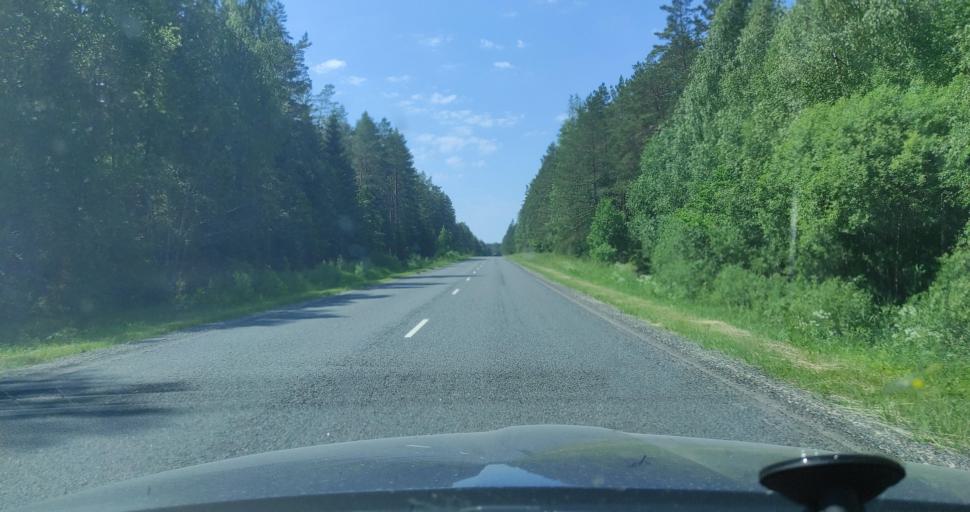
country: LV
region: Salacgrivas
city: Ainazi
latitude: 57.8544
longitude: 24.4742
